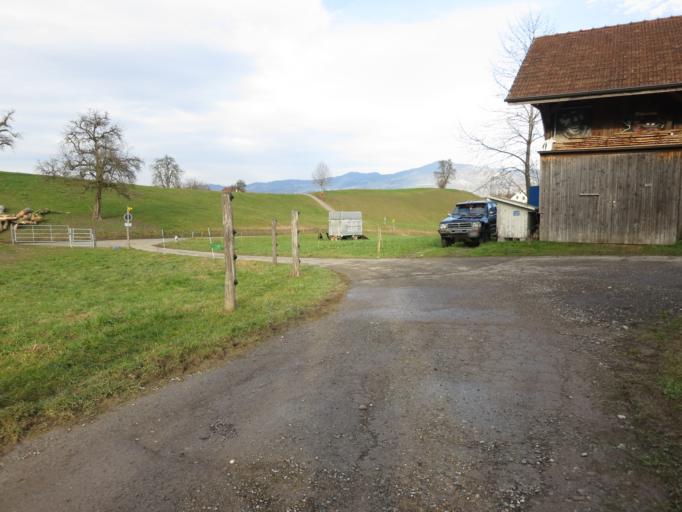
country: CH
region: Zurich
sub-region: Bezirk Hinwil
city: Bubikon
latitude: 47.2494
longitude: 8.8186
